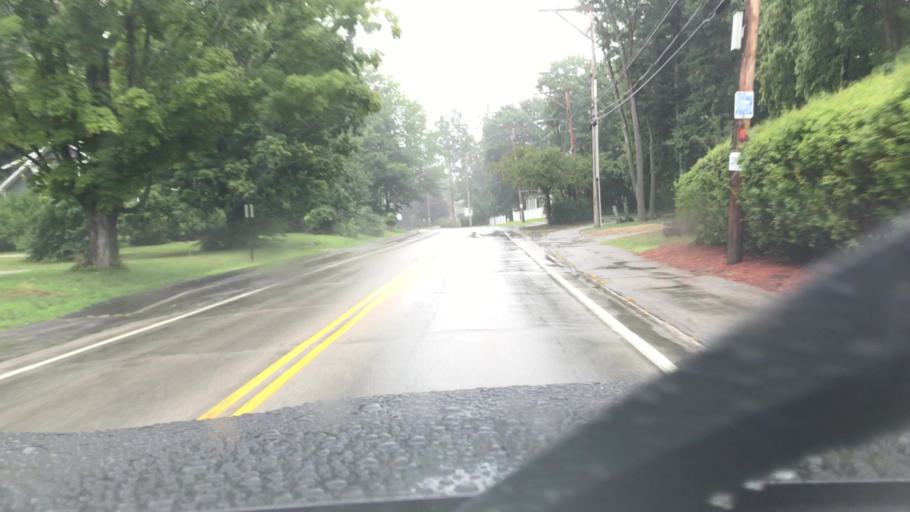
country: US
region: New Hampshire
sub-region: Strafford County
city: Durham
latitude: 43.1387
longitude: -70.9261
